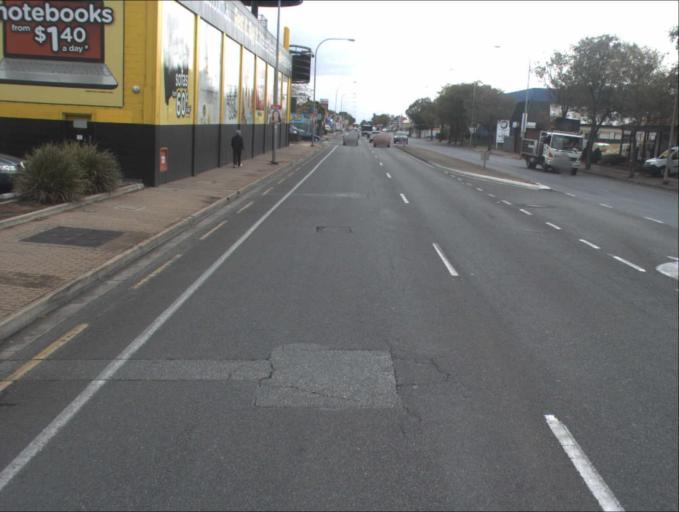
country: AU
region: South Australia
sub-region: Prospect
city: Prospect
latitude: -34.8904
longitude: 138.6032
